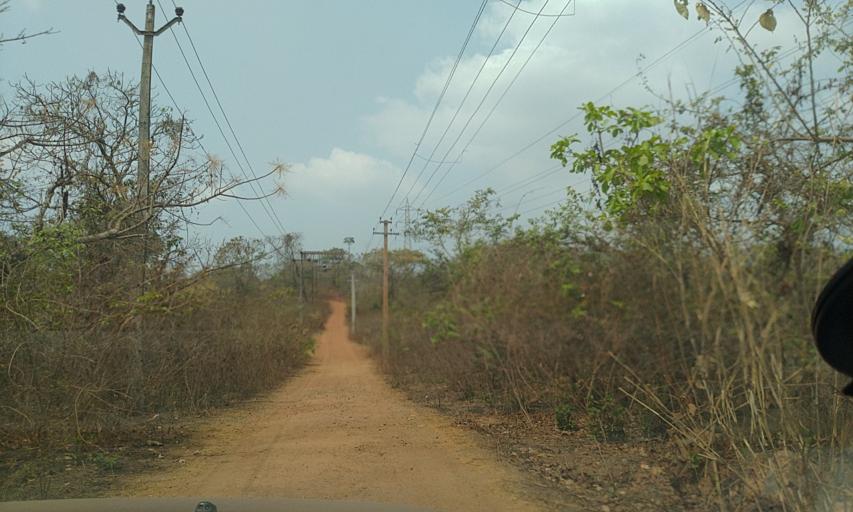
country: IN
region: Goa
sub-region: North Goa
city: Goa Velha
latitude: 15.4852
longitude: 73.9147
